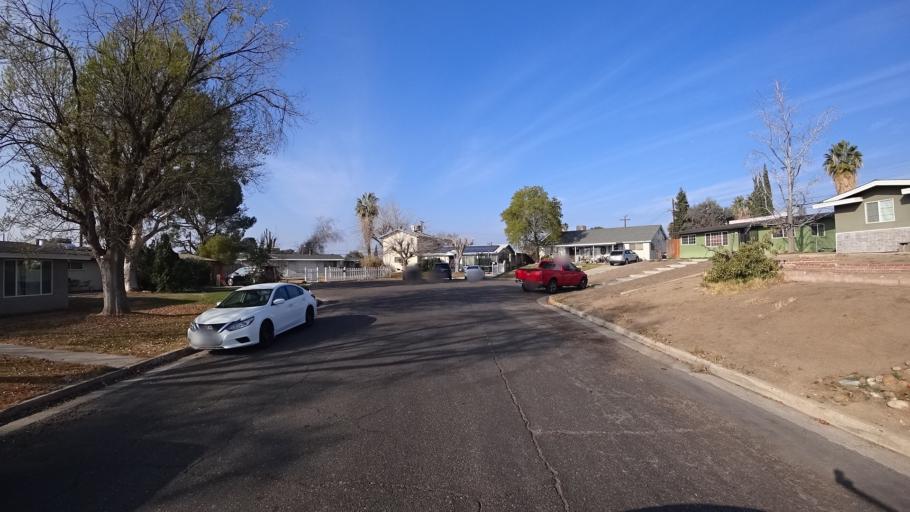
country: US
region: California
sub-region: Kern County
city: Oildale
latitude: 35.4040
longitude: -118.9839
